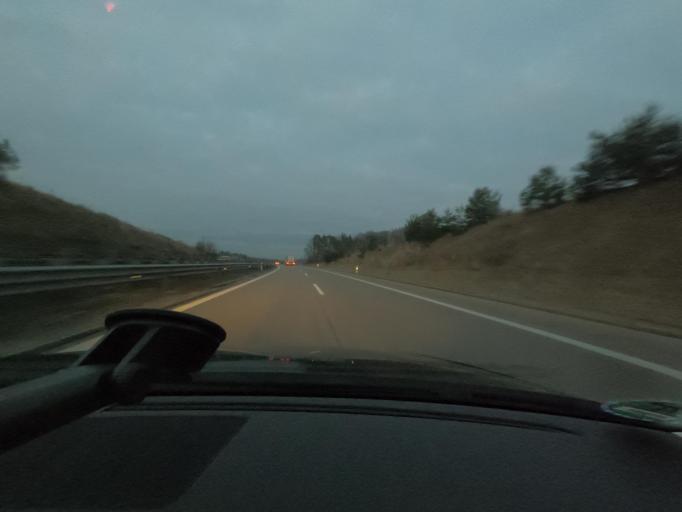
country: DE
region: Bavaria
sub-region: Upper Franconia
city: Lichtenfels
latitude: 50.1816
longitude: 11.0253
